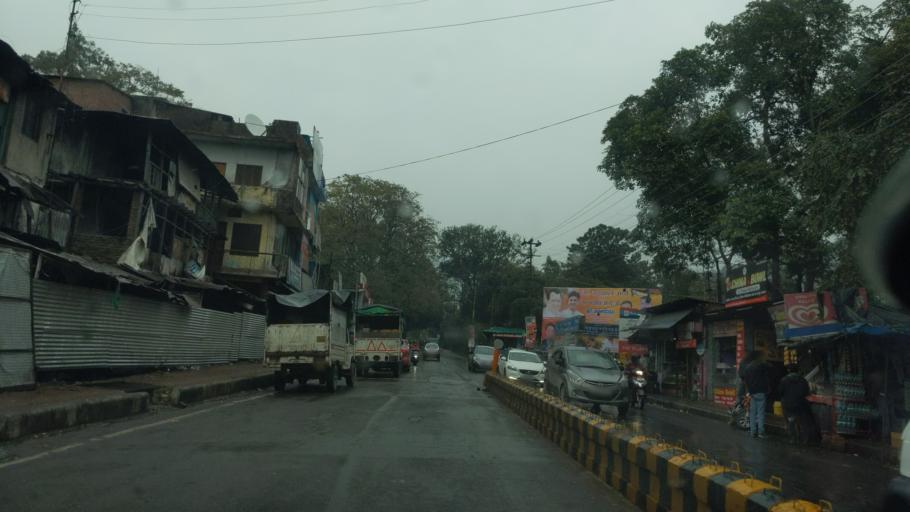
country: IN
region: Uttarakhand
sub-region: Naini Tal
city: Haldwani
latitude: 29.2649
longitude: 79.5446
